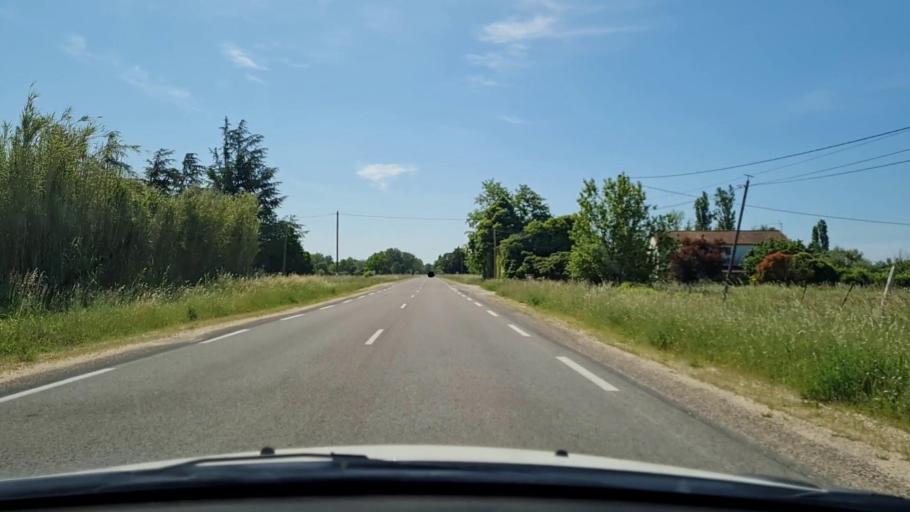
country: FR
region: Languedoc-Roussillon
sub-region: Departement du Gard
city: Saint-Genies-de-Malgoires
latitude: 43.9611
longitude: 4.2359
